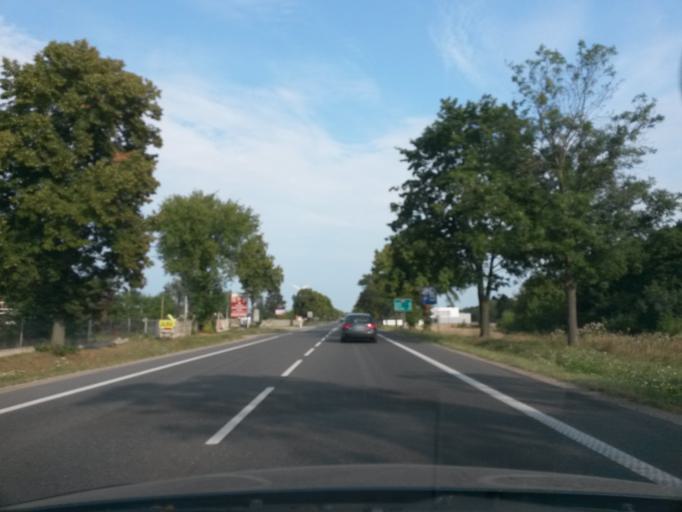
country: PL
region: Masovian Voivodeship
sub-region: Powiat sierpecki
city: Sierpc
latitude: 52.8520
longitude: 19.6953
